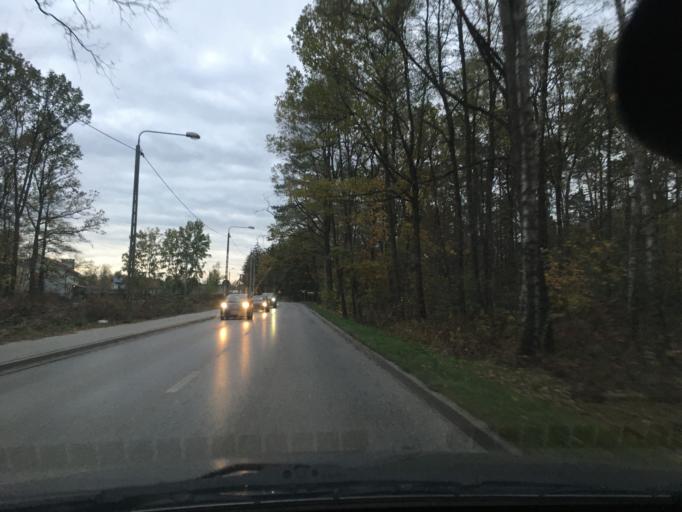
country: PL
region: Masovian Voivodeship
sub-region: Powiat piaseczynski
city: Lesznowola
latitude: 52.0784
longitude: 20.9372
